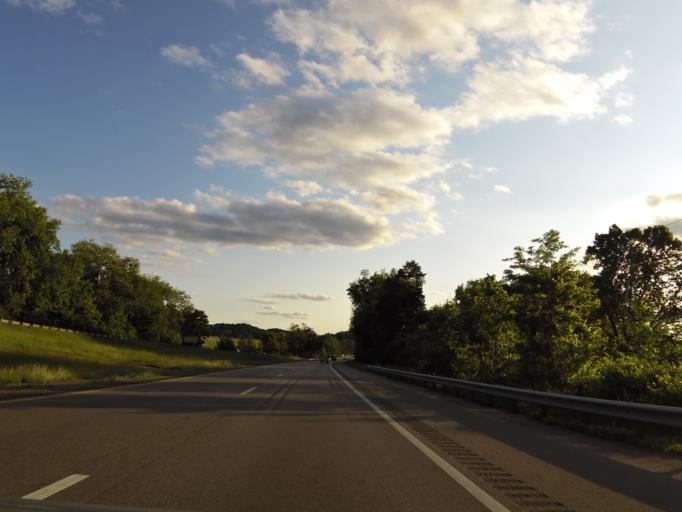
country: US
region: Tennessee
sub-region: Sullivan County
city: Fairmount
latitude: 36.6430
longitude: -82.0938
